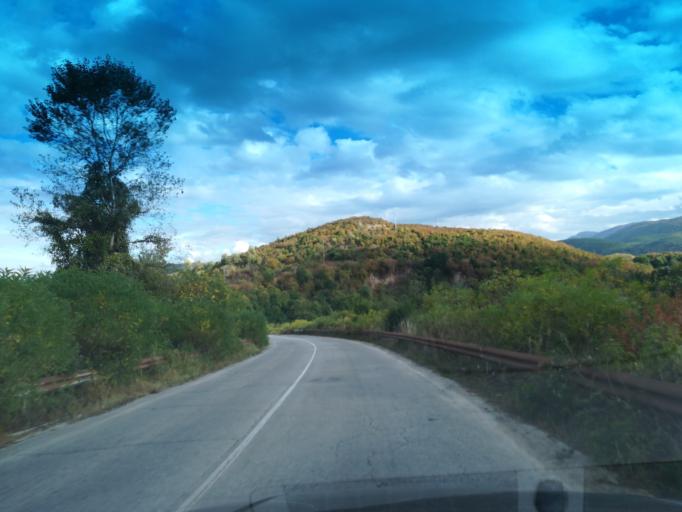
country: BG
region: Pazardzhik
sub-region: Obshtina Peshtera
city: Peshtera
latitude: 42.0465
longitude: 24.3284
